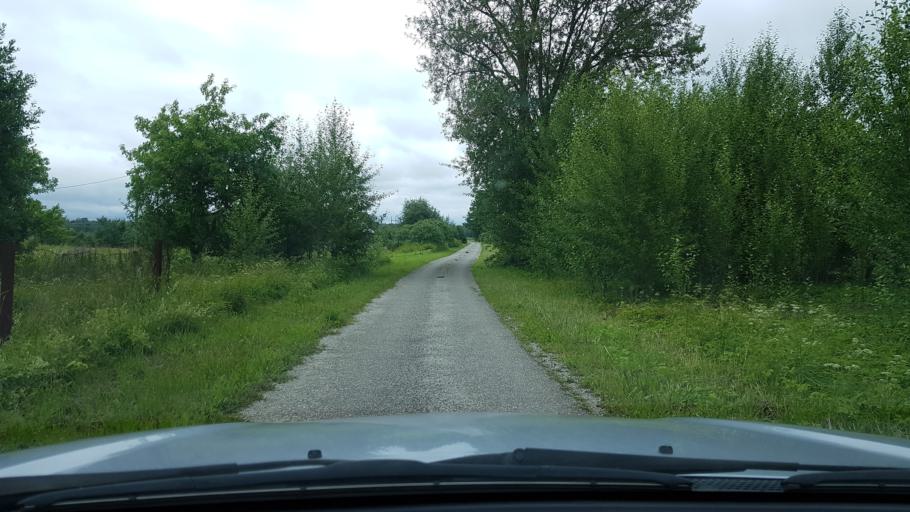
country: EE
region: Ida-Virumaa
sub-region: Narva-Joesuu linn
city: Narva-Joesuu
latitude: 59.3432
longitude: 27.9436
